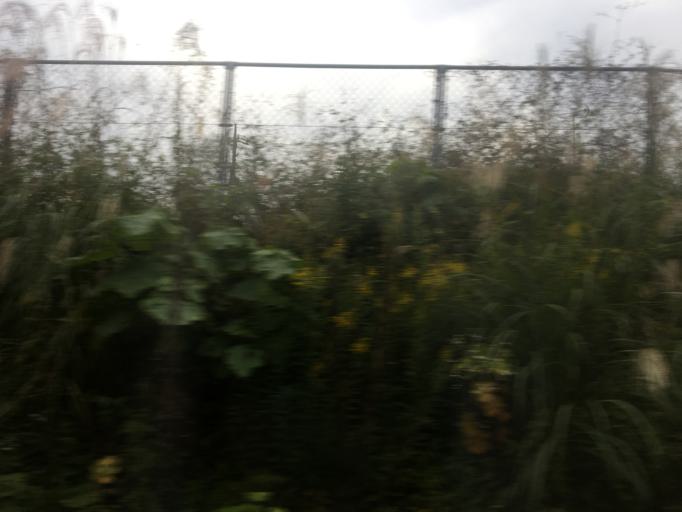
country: JP
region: Saitama
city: Sakado
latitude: 35.9015
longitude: 139.3670
